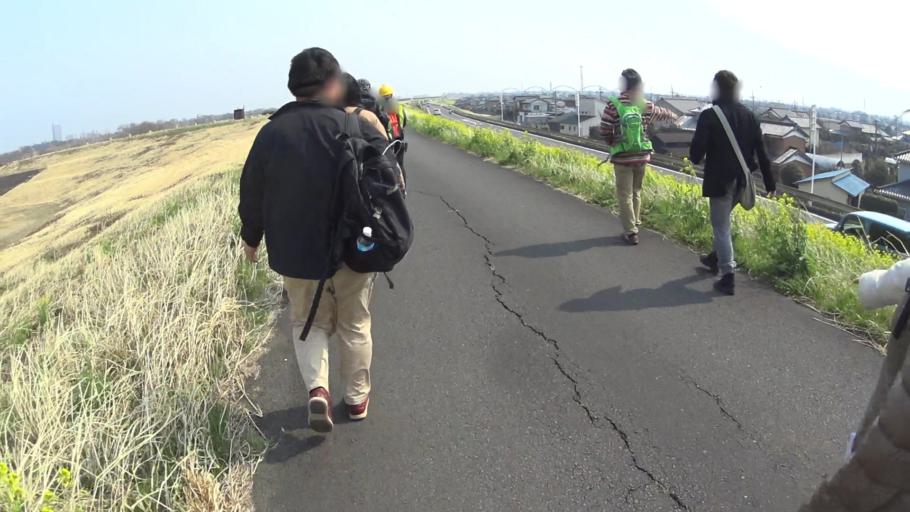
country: JP
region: Ibaraki
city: Koga
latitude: 36.1988
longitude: 139.6826
